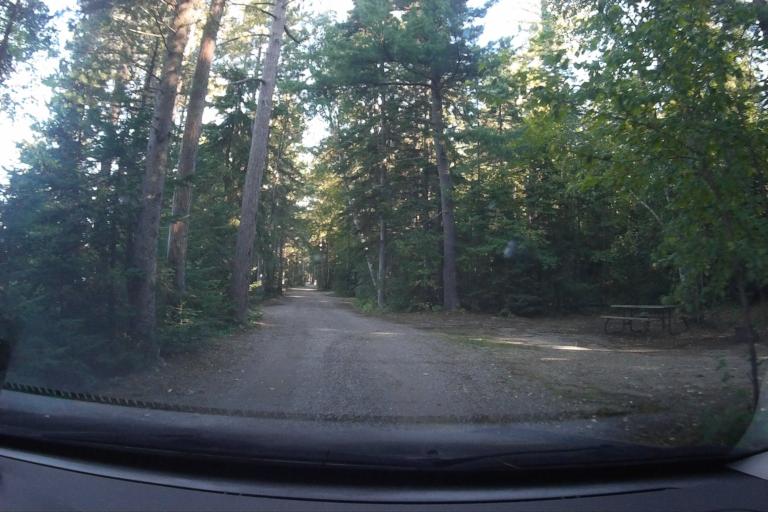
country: CA
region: Ontario
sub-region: Algoma
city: Sault Ste. Marie
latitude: 47.3243
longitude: -84.6107
